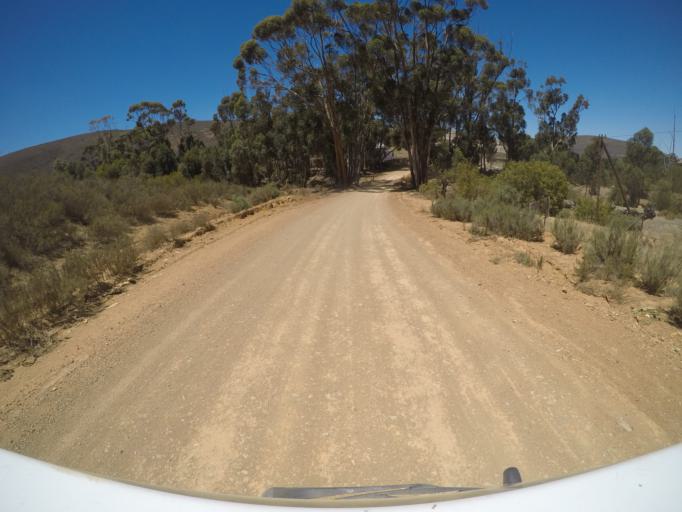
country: ZA
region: Western Cape
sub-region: Overberg District Municipality
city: Caledon
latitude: -34.1375
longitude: 19.2474
